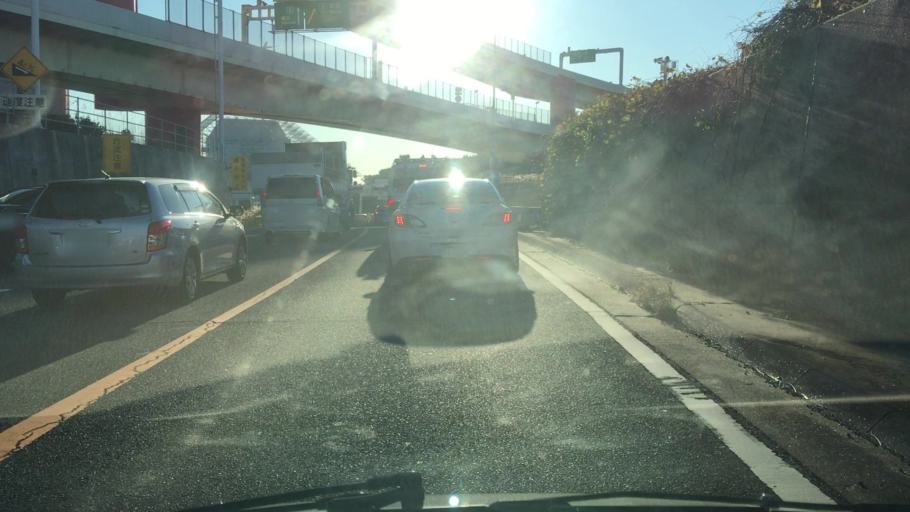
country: JP
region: Kanagawa
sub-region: Kawasaki-shi
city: Kawasaki
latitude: 35.5192
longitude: 139.7907
